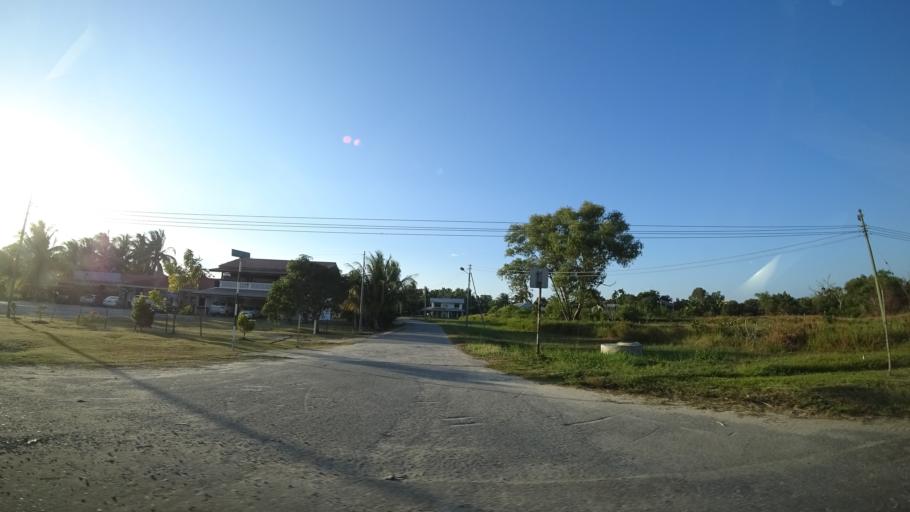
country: BN
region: Tutong
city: Tutong
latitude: 4.7309
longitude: 114.5564
